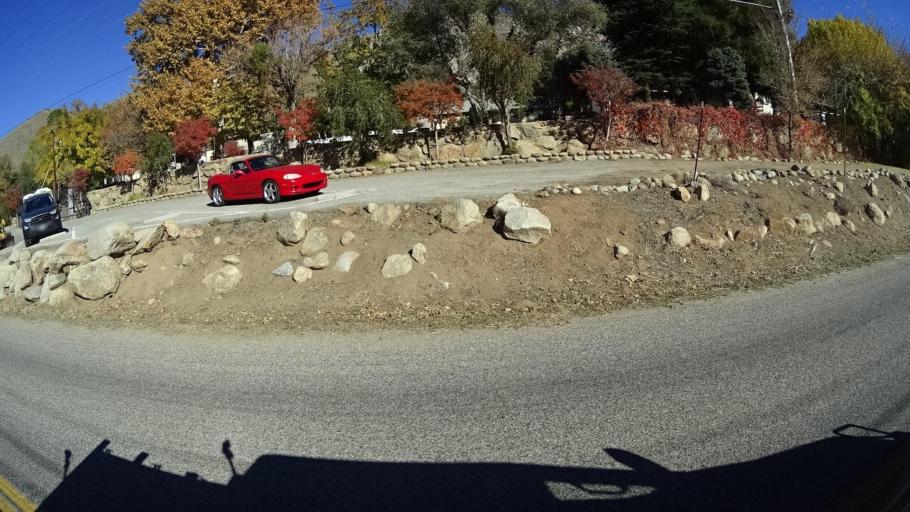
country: US
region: California
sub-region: Kern County
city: Kernville
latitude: 35.7689
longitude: -118.4293
